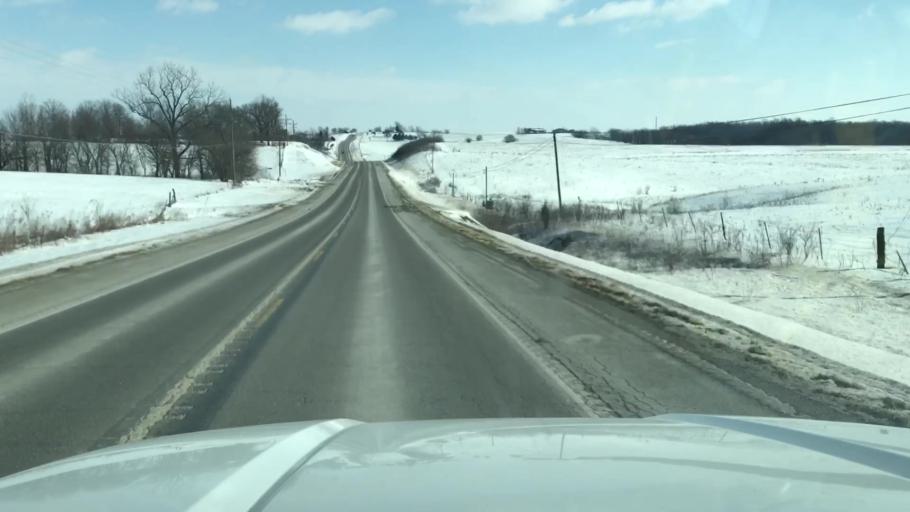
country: US
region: Missouri
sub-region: Nodaway County
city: Maryville
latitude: 40.3445
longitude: -94.7871
